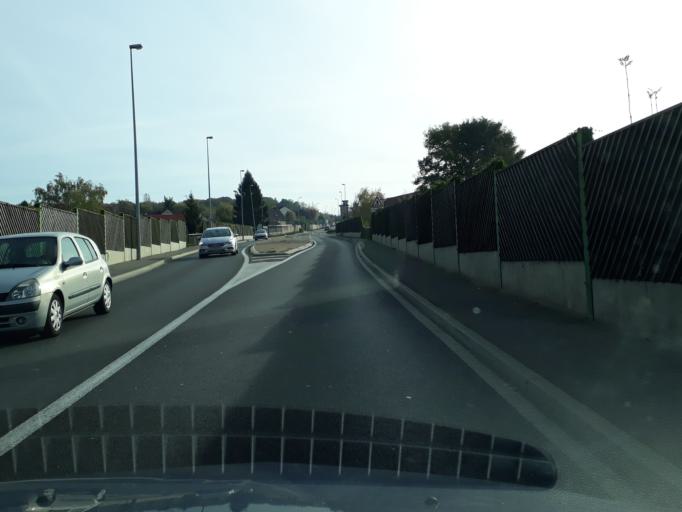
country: FR
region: Ile-de-France
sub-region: Departement de Seine-et-Marne
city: Samoreau
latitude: 48.4274
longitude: 2.7539
